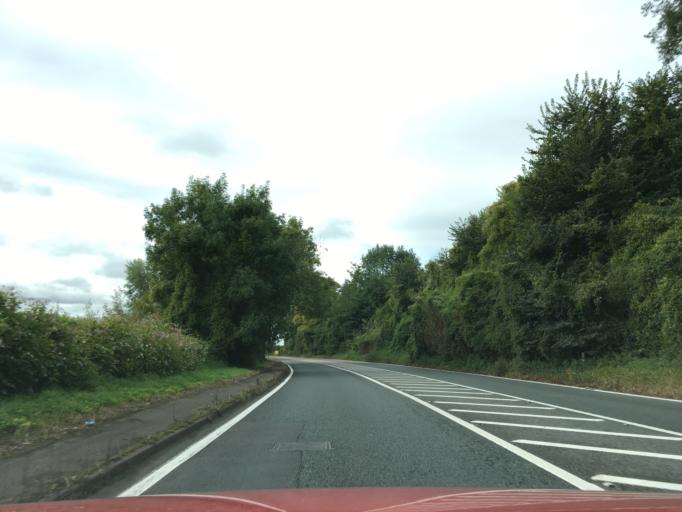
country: GB
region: England
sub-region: Gloucestershire
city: Newent
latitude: 51.8461
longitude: -2.3534
